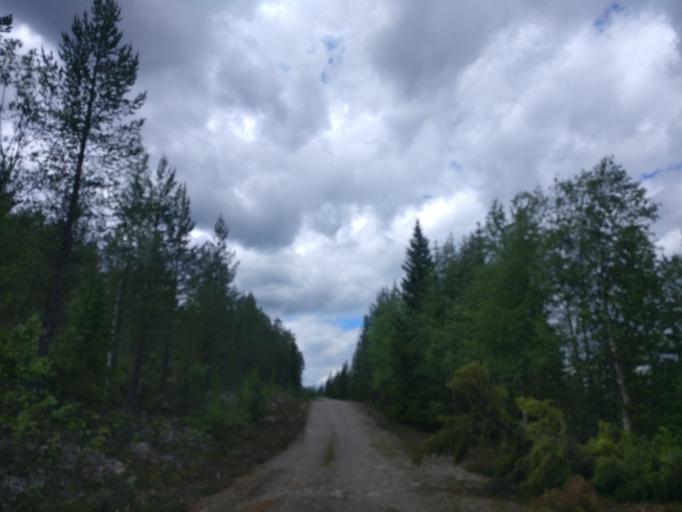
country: SE
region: Jaemtland
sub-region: Harjedalens Kommun
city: Sveg
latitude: 62.1972
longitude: 13.4113
